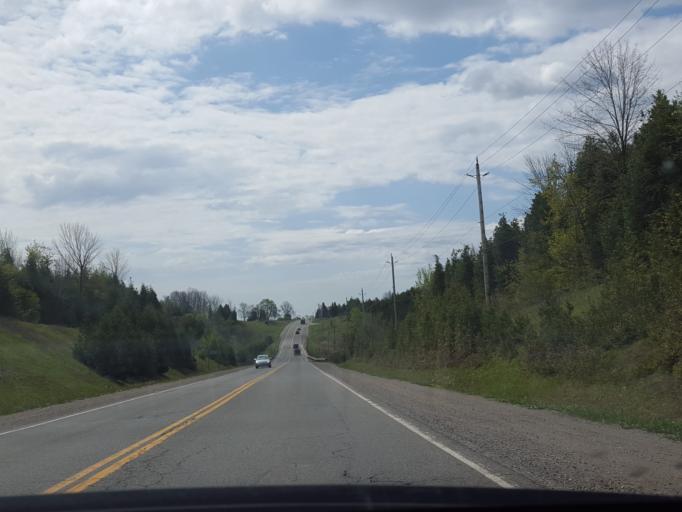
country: CA
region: Ontario
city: Oshawa
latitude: 43.9297
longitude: -78.7101
